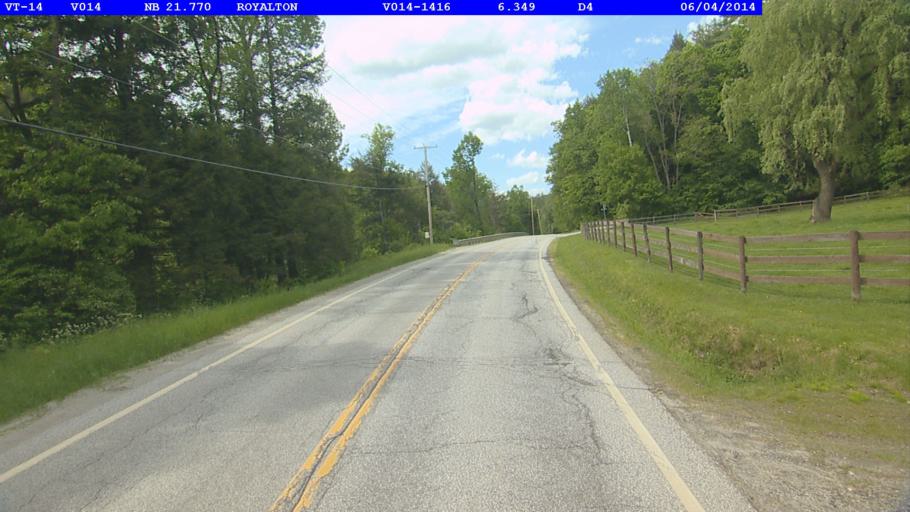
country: US
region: Vermont
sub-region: Orange County
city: Randolph
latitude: 43.8319
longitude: -72.5724
